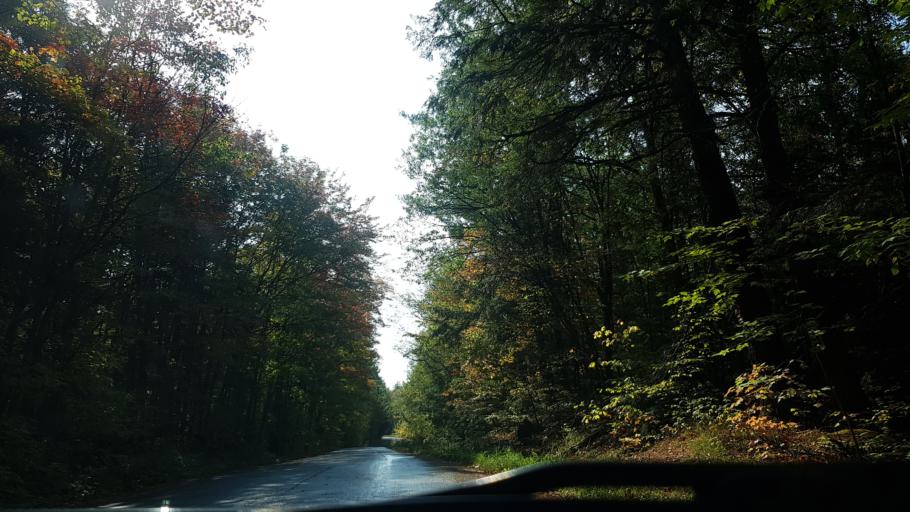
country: CA
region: Ontario
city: Bracebridge
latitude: 44.9823
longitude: -79.2627
